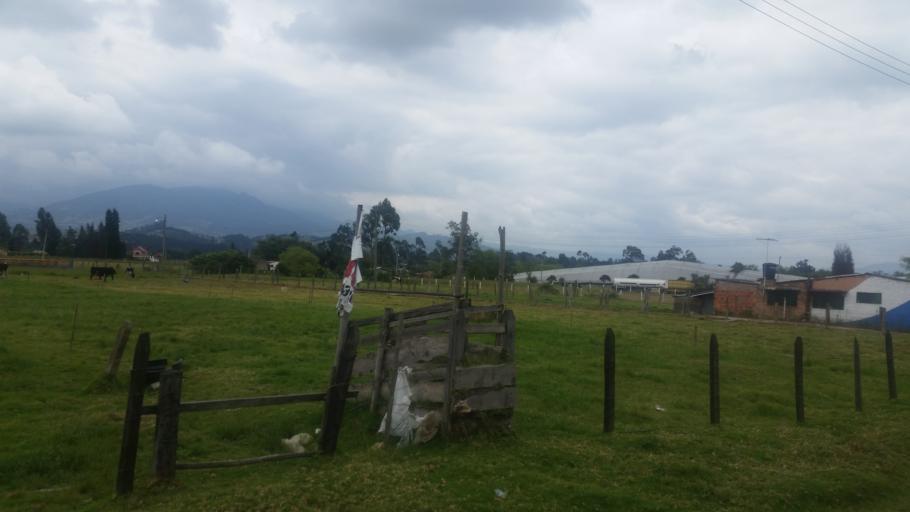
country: CO
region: Cundinamarca
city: Cogua
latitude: 5.0423
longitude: -73.9526
